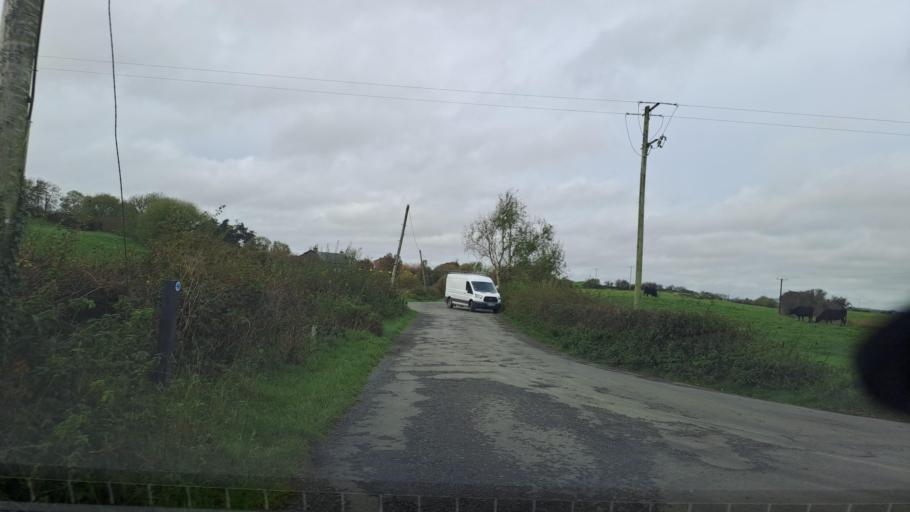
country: IE
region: Ulster
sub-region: An Cabhan
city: Kingscourt
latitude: 54.0227
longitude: -6.8264
